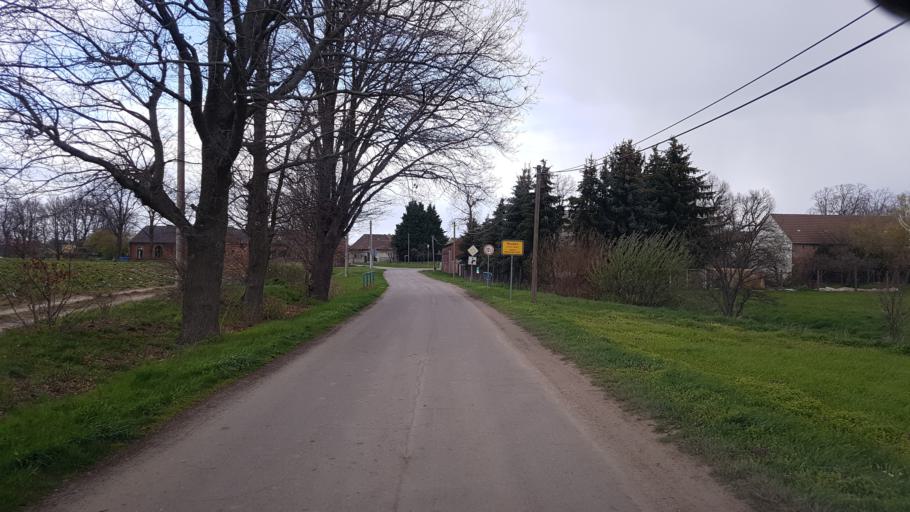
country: DE
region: Brandenburg
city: Calau
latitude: 51.7525
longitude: 14.0035
